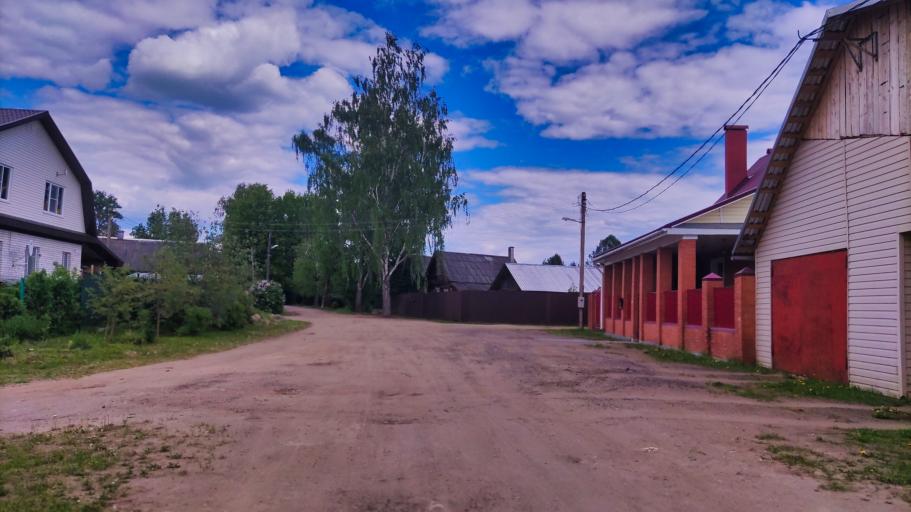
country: RU
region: Tverskaya
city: Rzhev
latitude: 56.2483
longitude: 34.2942
